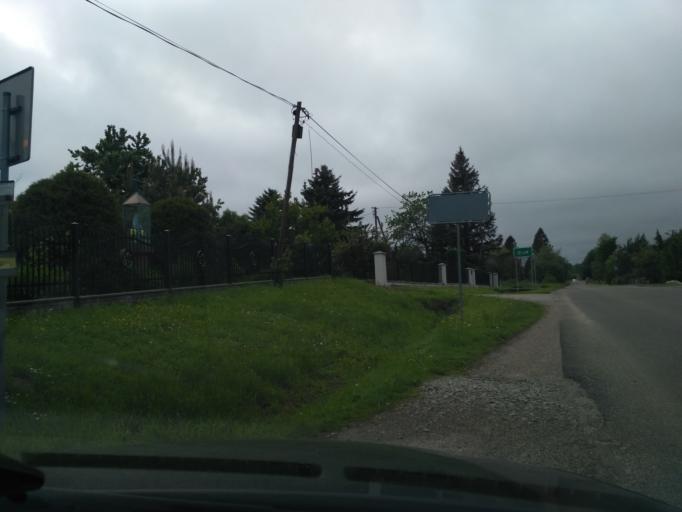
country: PL
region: Subcarpathian Voivodeship
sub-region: Powiat jasielski
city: Brzyska
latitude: 49.8104
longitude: 21.4002
